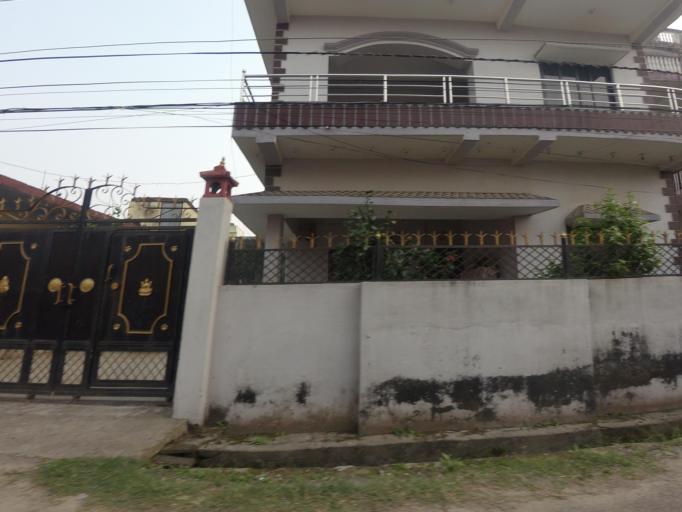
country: NP
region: Western Region
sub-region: Lumbini Zone
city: Bhairahawa
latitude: 27.5166
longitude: 83.4484
